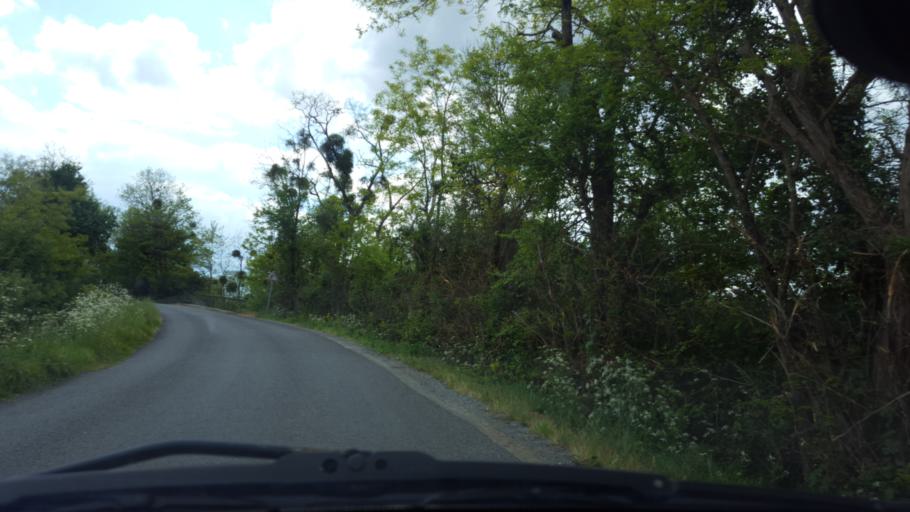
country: FR
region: Pays de la Loire
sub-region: Departement de la Loire-Atlantique
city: Saint-Philbert-de-Grand-Lieu
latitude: 47.0374
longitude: -1.6023
